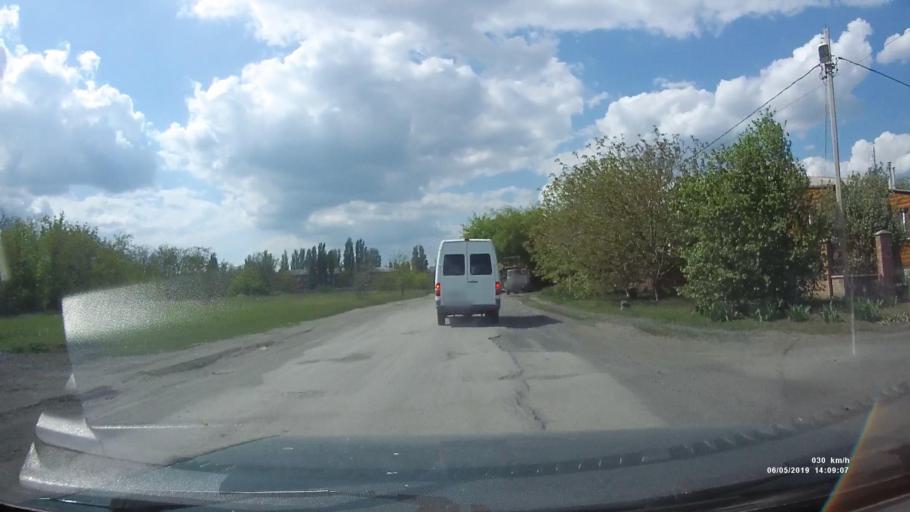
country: RU
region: Rostov
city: Shakhty
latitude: 47.6855
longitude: 40.2928
